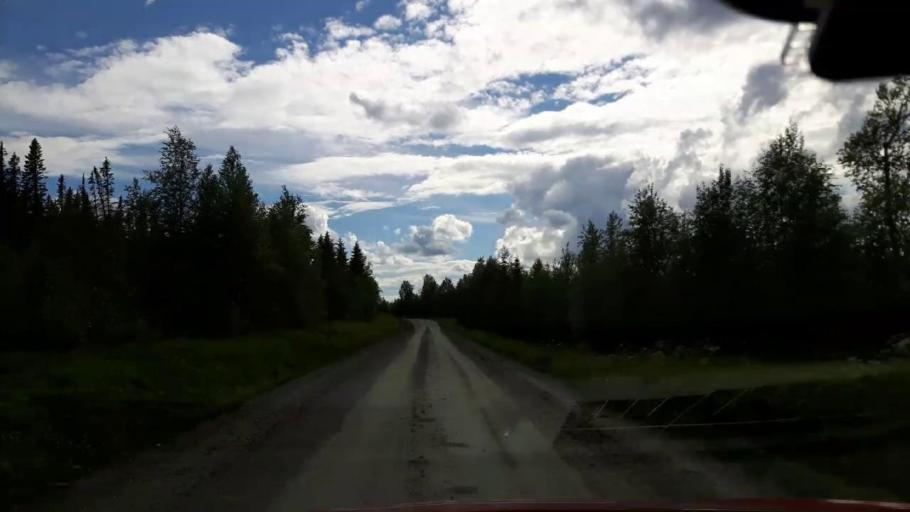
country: SE
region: Jaemtland
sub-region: Krokoms Kommun
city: Valla
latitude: 63.8874
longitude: 14.1512
